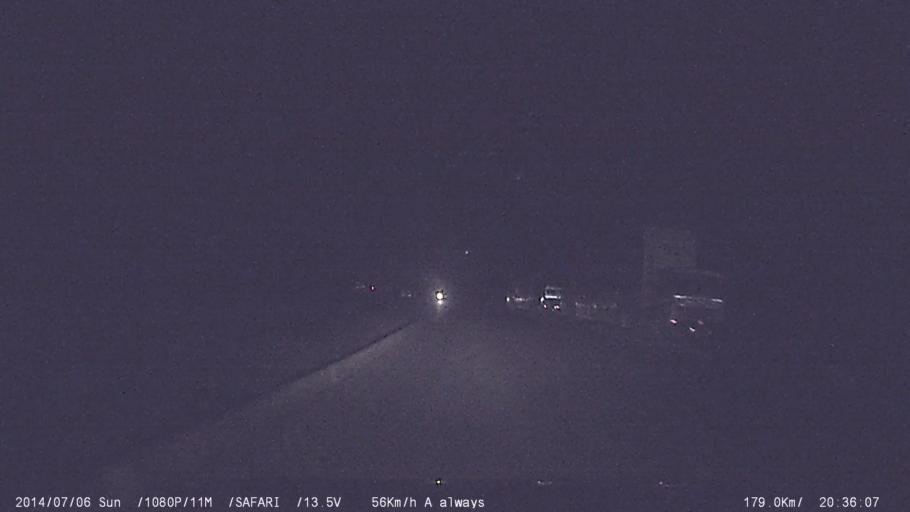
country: IN
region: Kerala
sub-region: Palakkad district
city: Chittur
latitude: 10.8169
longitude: 76.8038
